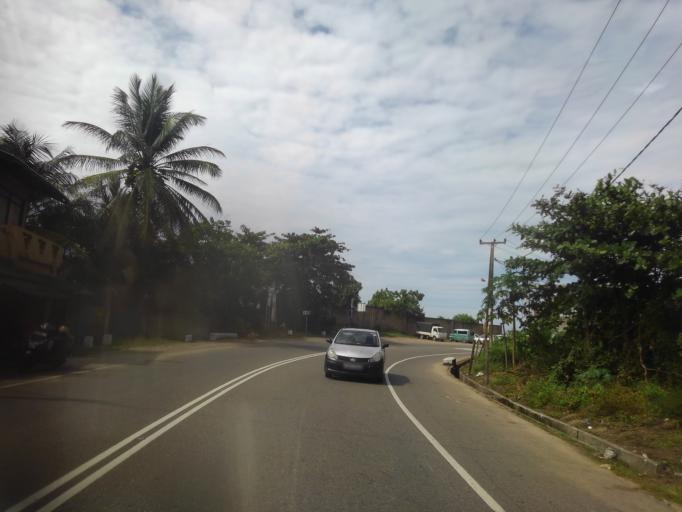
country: LK
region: Southern
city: Hikkaduwa
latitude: 6.1440
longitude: 80.0995
